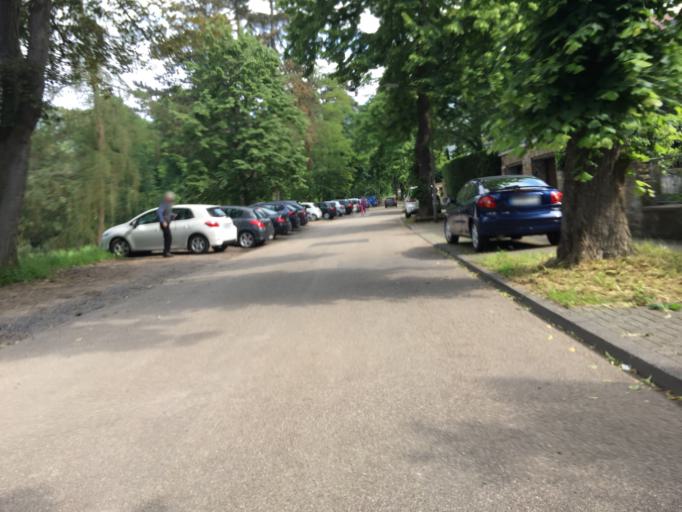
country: DE
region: Hesse
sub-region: Regierungsbezirk Darmstadt
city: Wiesbaden
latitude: 50.0924
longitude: 8.2591
